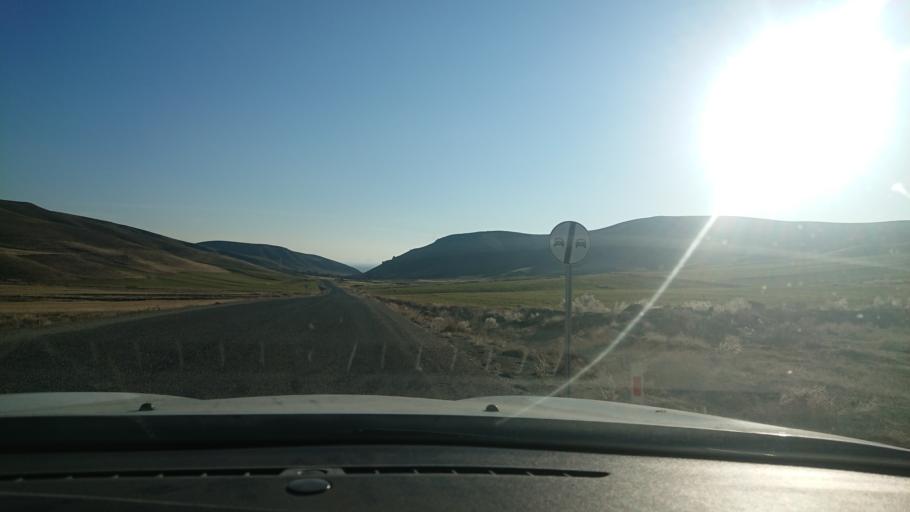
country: TR
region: Aksaray
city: Acipinar
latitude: 38.7006
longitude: 33.7527
